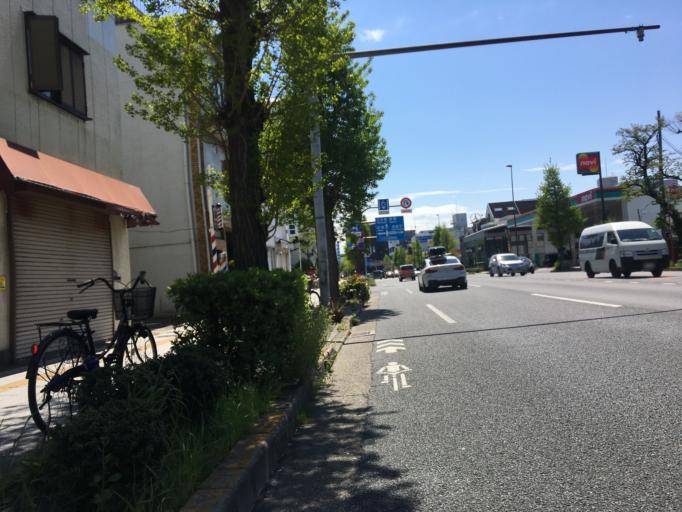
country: JP
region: Saitama
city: Shimotoda
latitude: 35.7875
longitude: 139.6851
